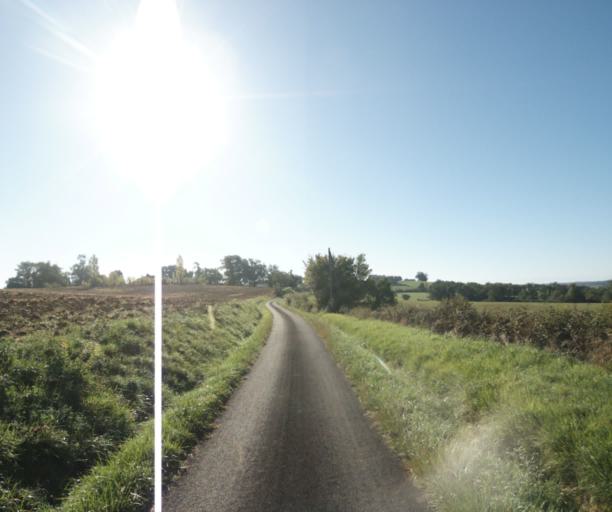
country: FR
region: Midi-Pyrenees
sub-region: Departement du Gers
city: Gondrin
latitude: 43.8269
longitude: 0.2578
